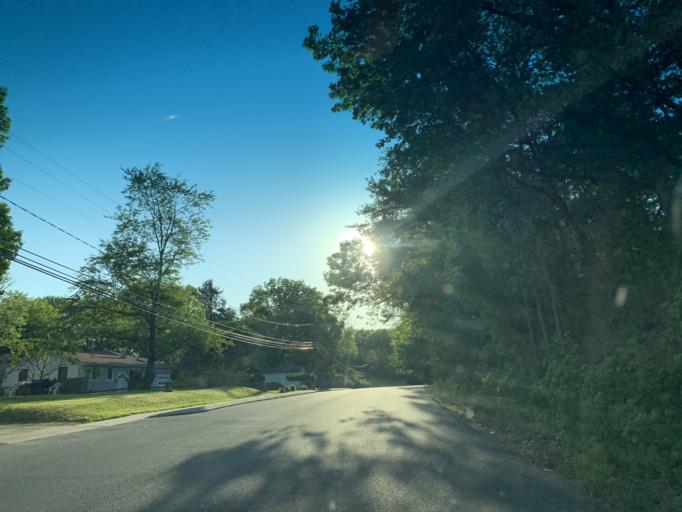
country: US
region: Maryland
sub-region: Harford County
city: Aberdeen
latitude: 39.5220
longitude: -76.1917
